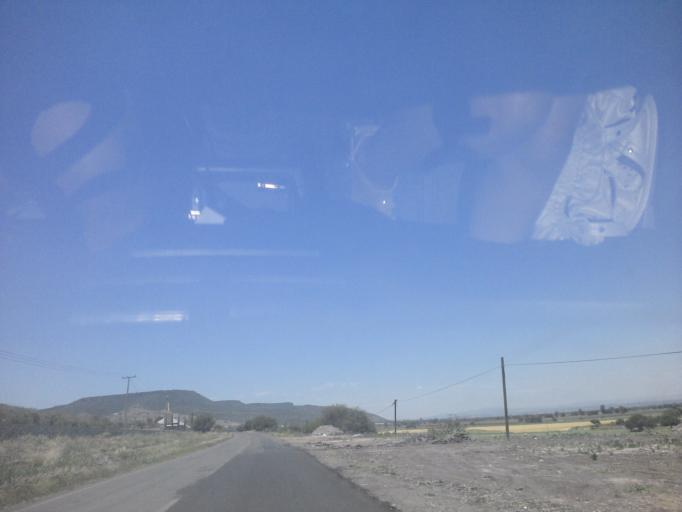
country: MX
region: Guanajuato
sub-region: San Francisco del Rincon
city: San Ignacio de Hidalgo
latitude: 20.9103
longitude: -101.9169
